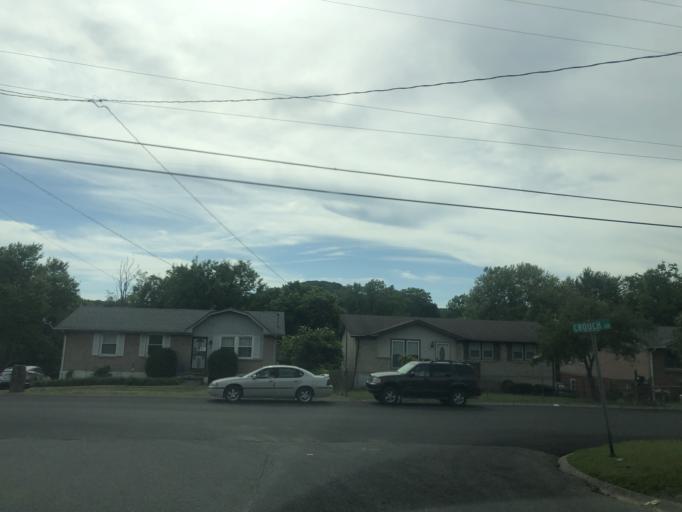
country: US
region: Tennessee
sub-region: Davidson County
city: Nashville
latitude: 36.2225
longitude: -86.8185
